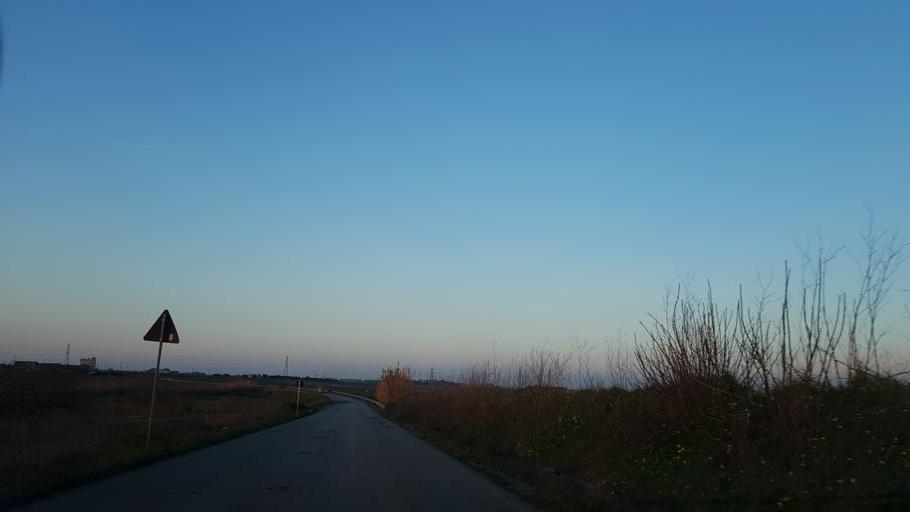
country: IT
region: Apulia
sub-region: Provincia di Brindisi
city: La Rosa
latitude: 40.5773
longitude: 17.9498
